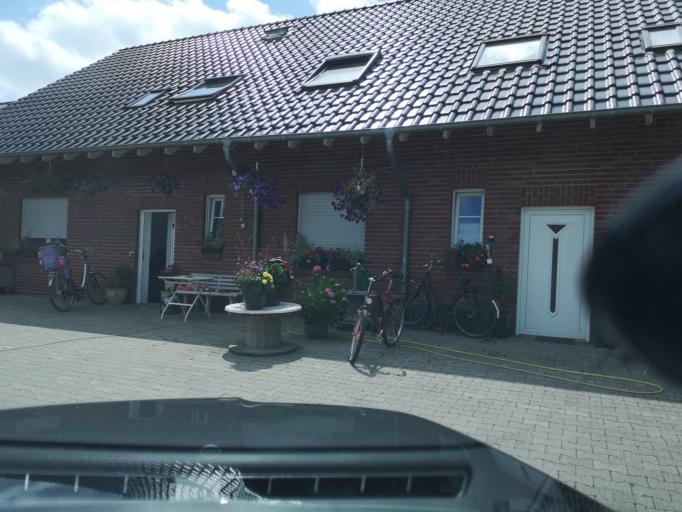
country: DE
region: North Rhine-Westphalia
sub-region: Regierungsbezirk Munster
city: Rhede
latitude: 51.8408
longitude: 6.6817
